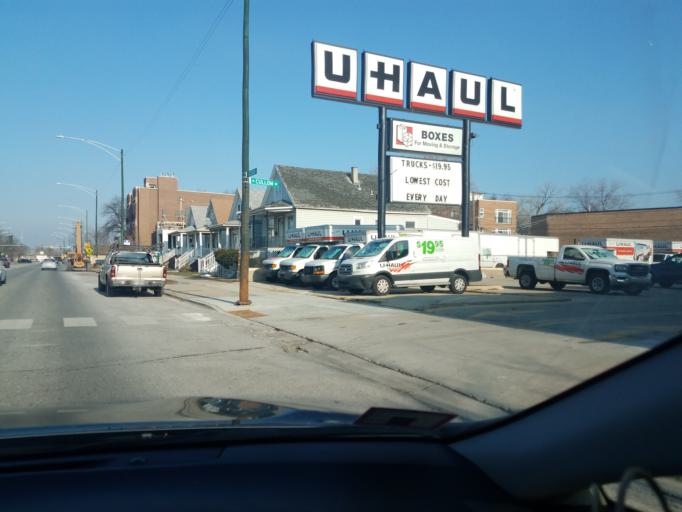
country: US
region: Illinois
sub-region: Cook County
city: Lincolnwood
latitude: 41.9589
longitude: -87.7474
